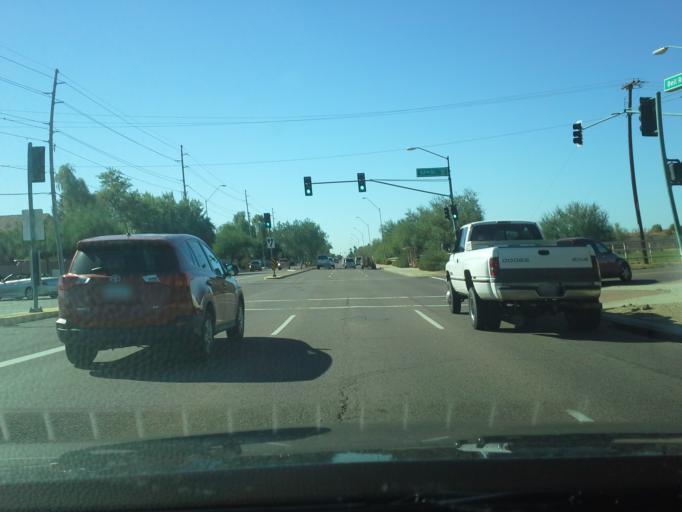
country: US
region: Arizona
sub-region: Maricopa County
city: Paradise Valley
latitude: 33.6406
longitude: -111.9682
